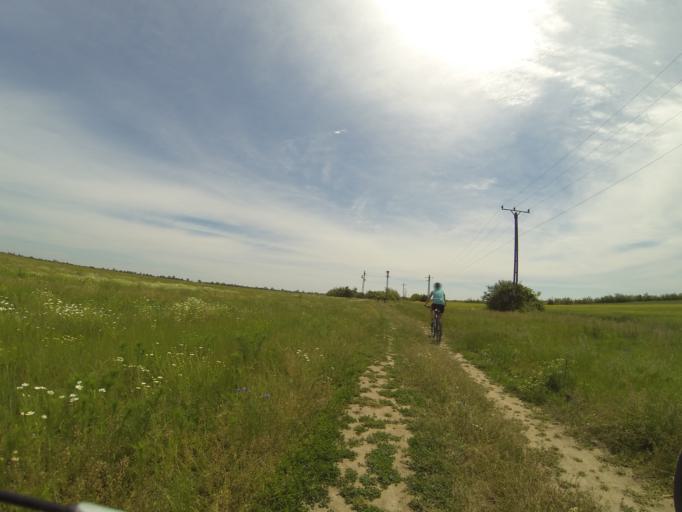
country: RO
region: Dolj
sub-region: Comuna Leu
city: Leu
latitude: 44.2042
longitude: 23.9657
